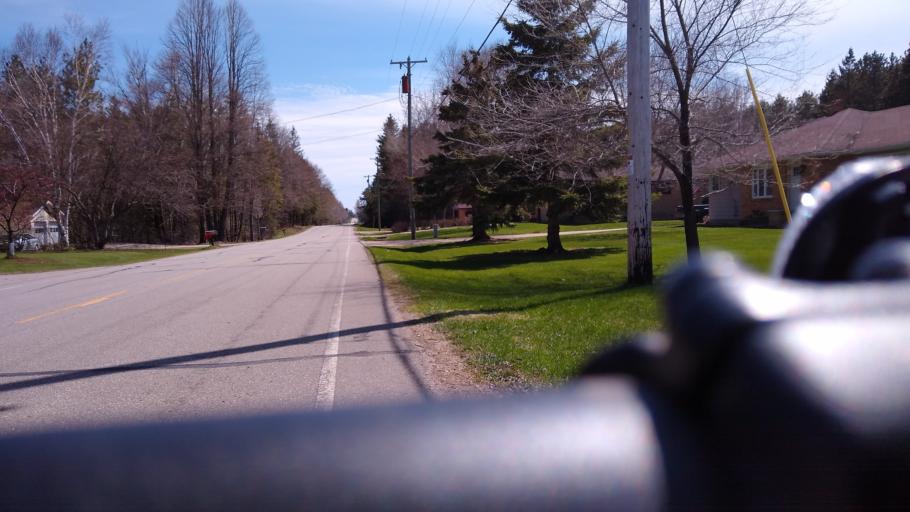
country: US
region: Michigan
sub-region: Delta County
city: Escanaba
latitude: 45.7320
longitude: -87.2025
